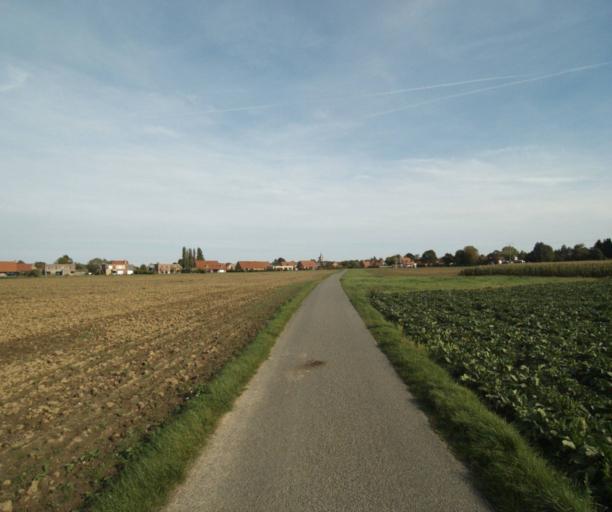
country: FR
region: Nord-Pas-de-Calais
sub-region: Departement du Nord
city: Fournes-en-Weppes
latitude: 50.5859
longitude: 2.8771
